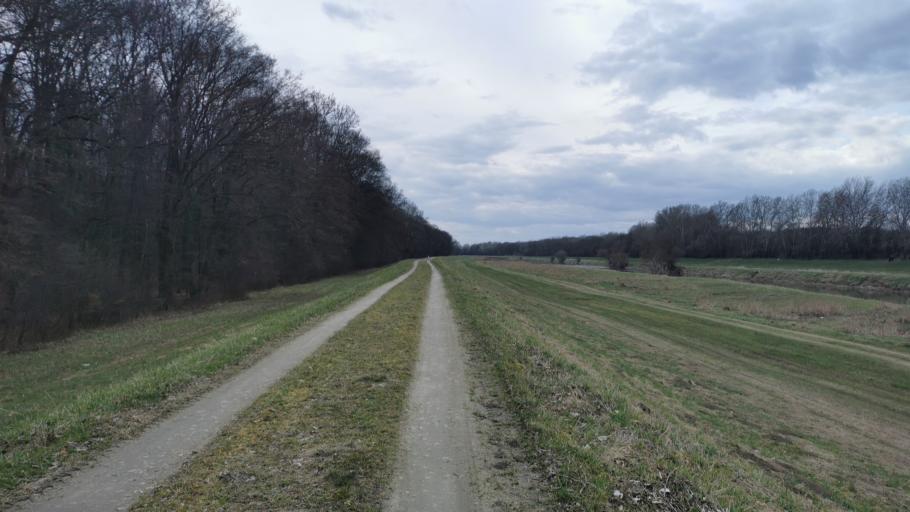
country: CZ
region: South Moravian
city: Hodonin
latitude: 48.8357
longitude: 17.1253
